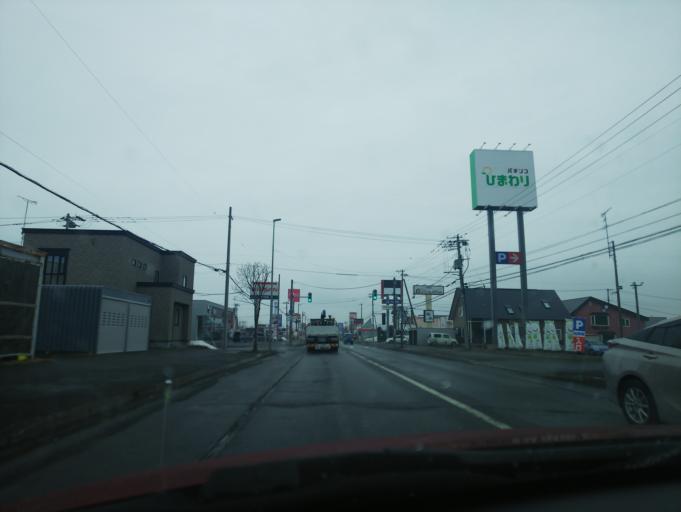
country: JP
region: Hokkaido
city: Nayoro
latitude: 44.1632
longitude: 142.3962
